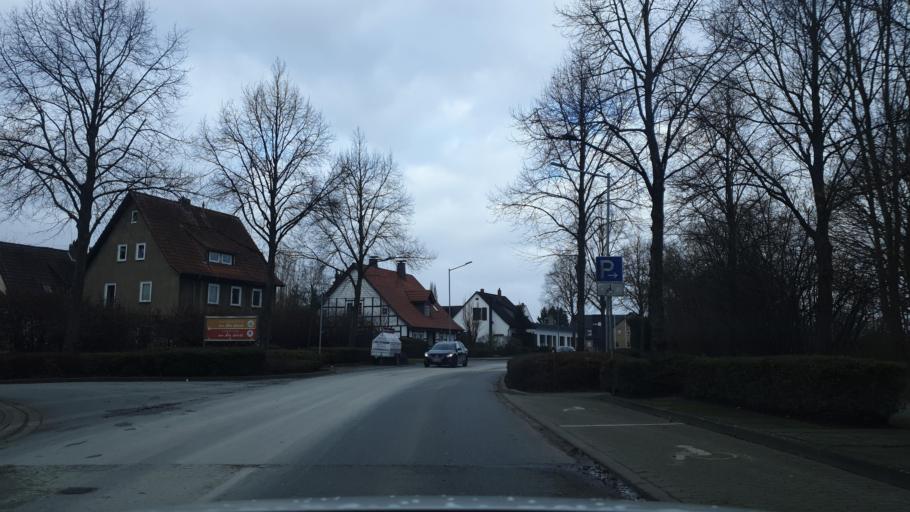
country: DE
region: North Rhine-Westphalia
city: Loehne
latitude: 52.2014
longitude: 8.7154
